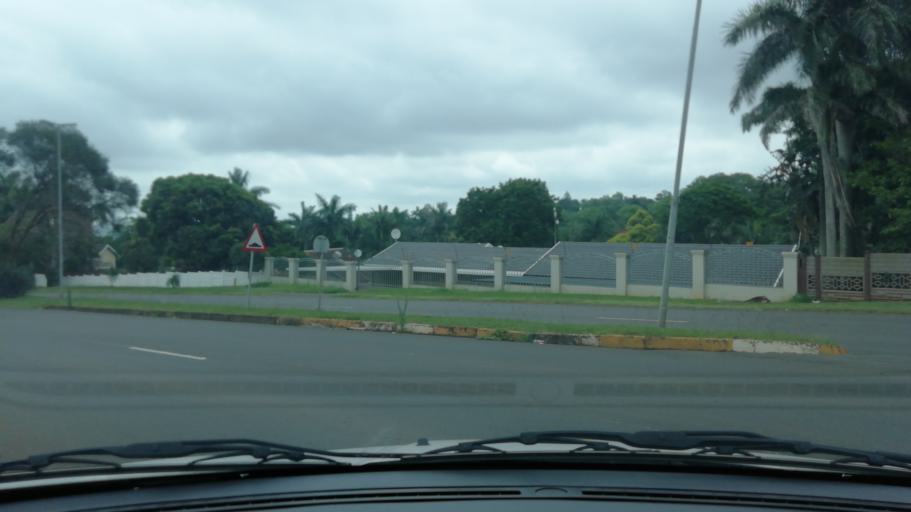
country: ZA
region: KwaZulu-Natal
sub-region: uThungulu District Municipality
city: Empangeni
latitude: -28.7656
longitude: 31.8956
